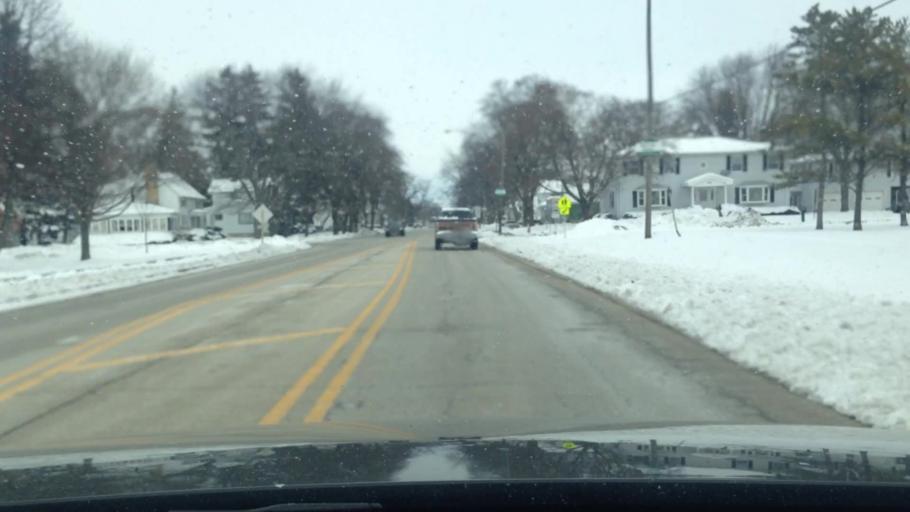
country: US
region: Illinois
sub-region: McHenry County
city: Hebron
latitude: 42.4656
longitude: -88.4328
